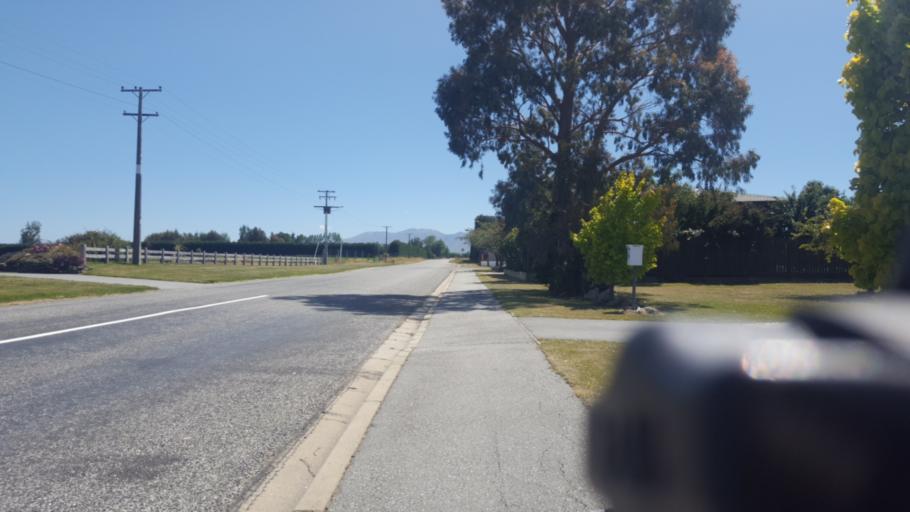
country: NZ
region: Otago
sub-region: Dunedin City
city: Dunedin
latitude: -45.1256
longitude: 170.1062
